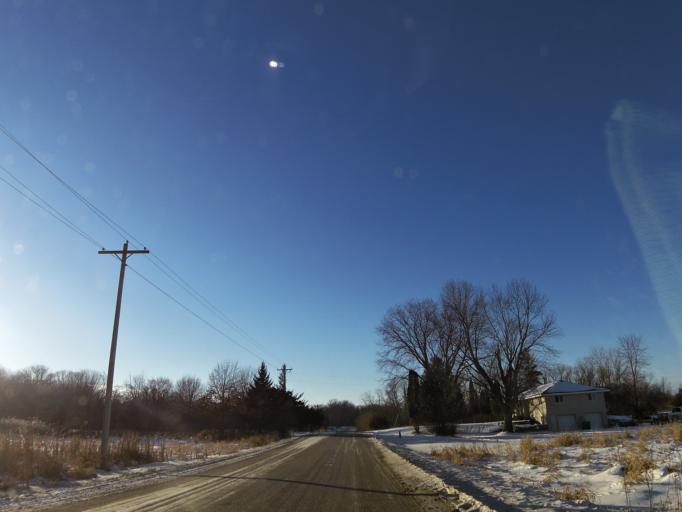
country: US
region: Minnesota
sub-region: Hennepin County
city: Mound
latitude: 44.9568
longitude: -93.6867
